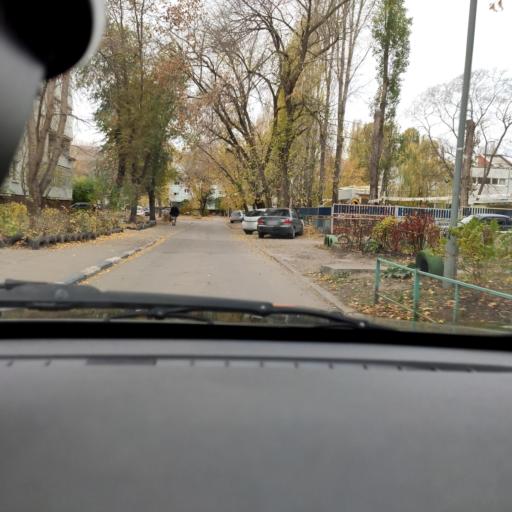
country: RU
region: Samara
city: Tol'yatti
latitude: 53.5347
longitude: 49.2962
